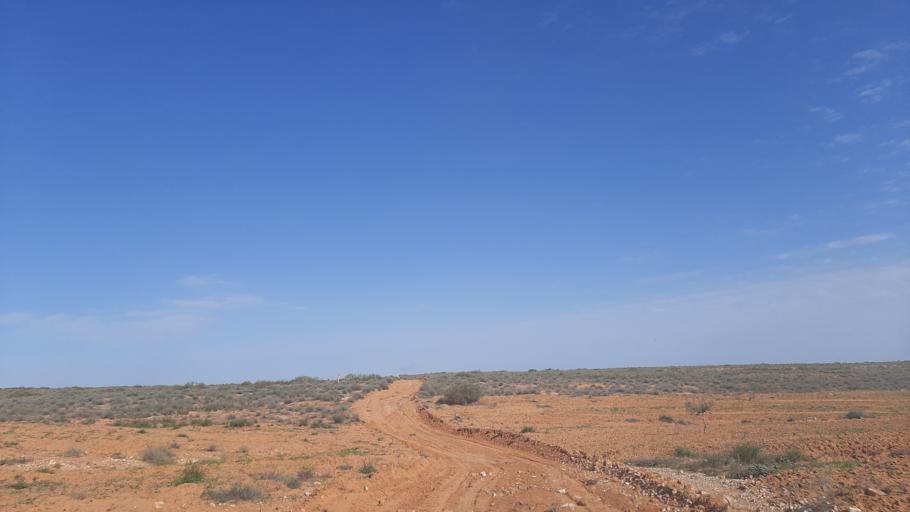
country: TN
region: Madanin
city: Medenine
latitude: 33.2470
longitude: 10.7455
